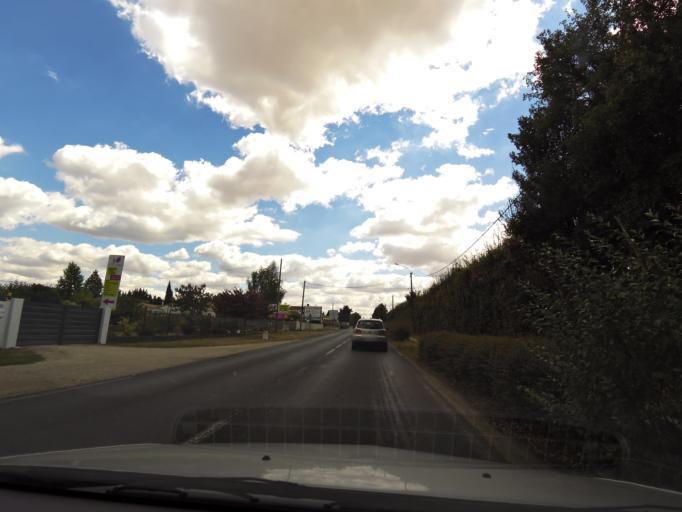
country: FR
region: Poitou-Charentes
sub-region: Departement des Deux-Sevres
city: Beauvoir-sur-Niort
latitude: 46.1862
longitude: -0.4737
